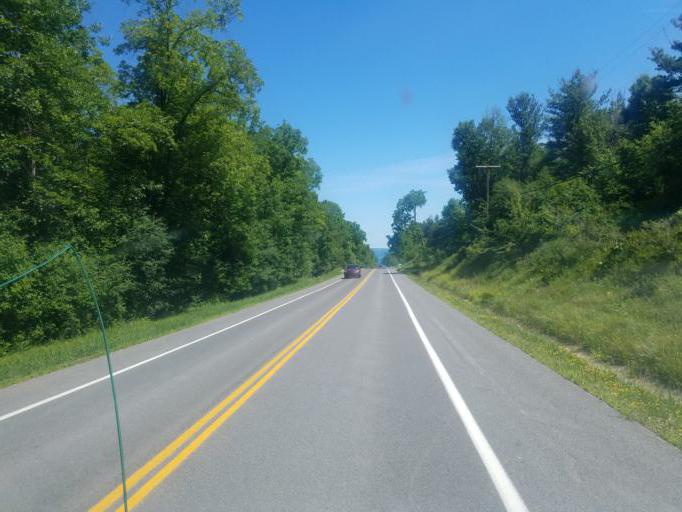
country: US
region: New York
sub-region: Ontario County
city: Canandaigua
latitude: 42.7648
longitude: -77.2983
